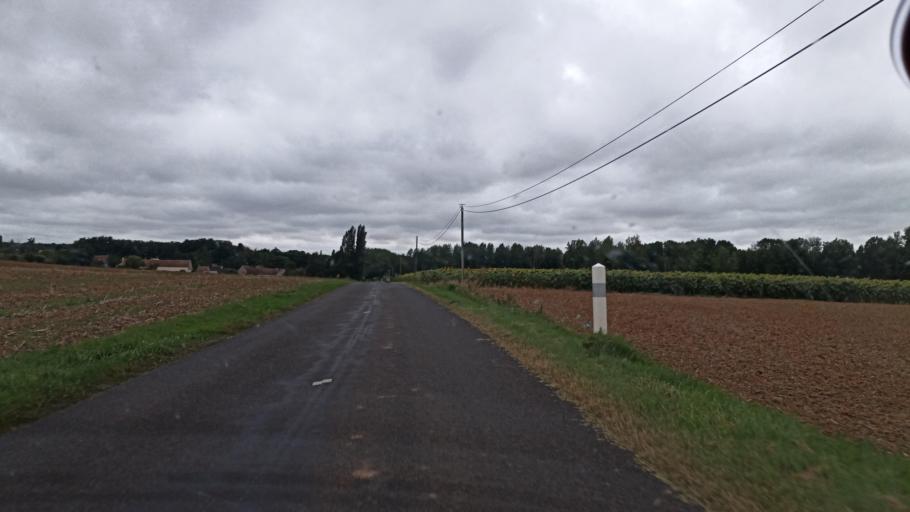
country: FR
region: Bourgogne
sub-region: Departement de l'Yonne
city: Cheroy
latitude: 48.2533
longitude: 3.0261
